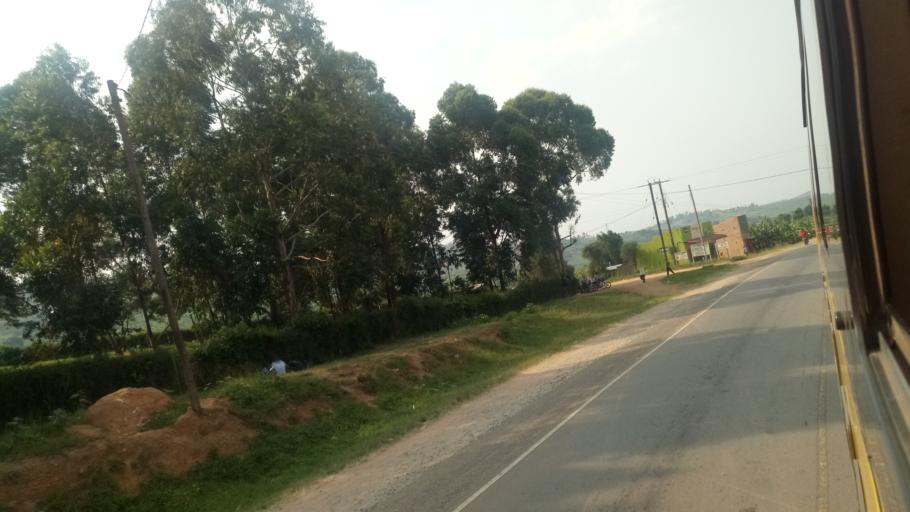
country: UG
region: Western Region
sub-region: Mbarara District
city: Mbarara
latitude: -0.5324
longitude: 30.7173
